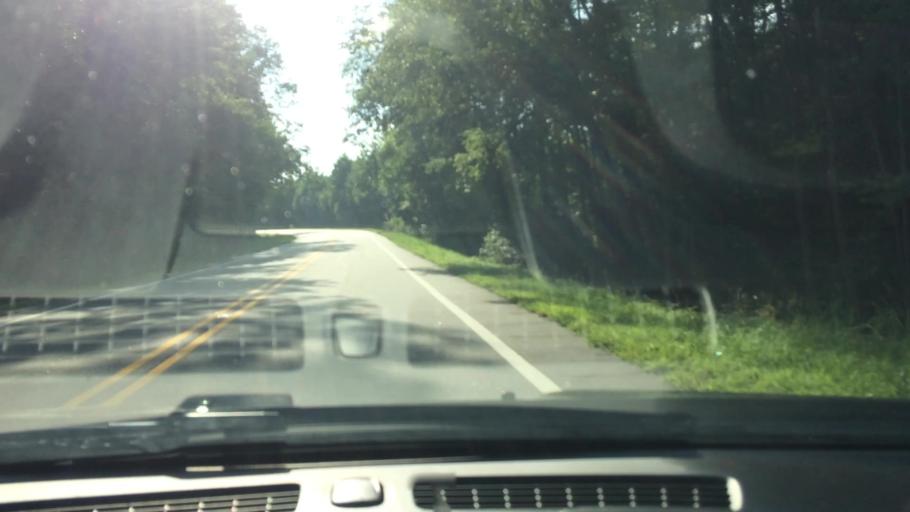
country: US
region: North Carolina
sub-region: Craven County
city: Vanceboro
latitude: 35.4293
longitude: -77.1900
